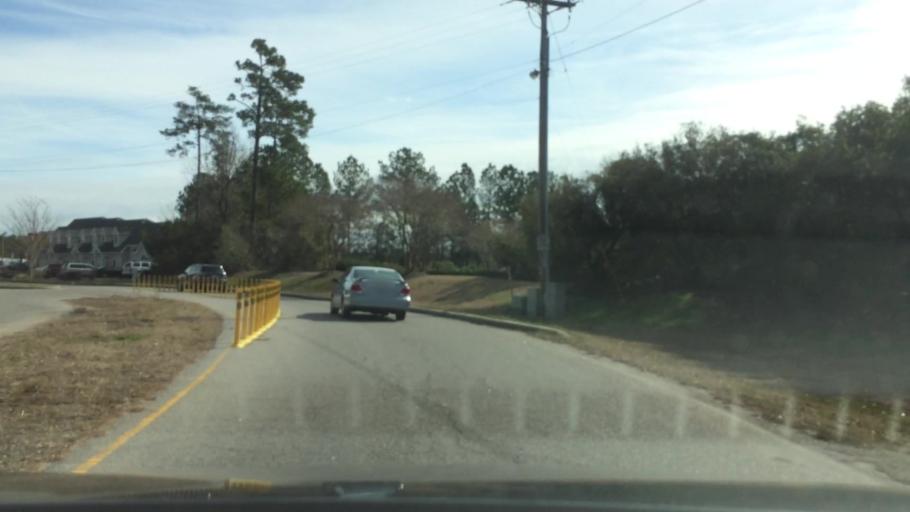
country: US
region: South Carolina
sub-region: Horry County
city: Socastee
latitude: 33.6785
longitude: -78.9679
